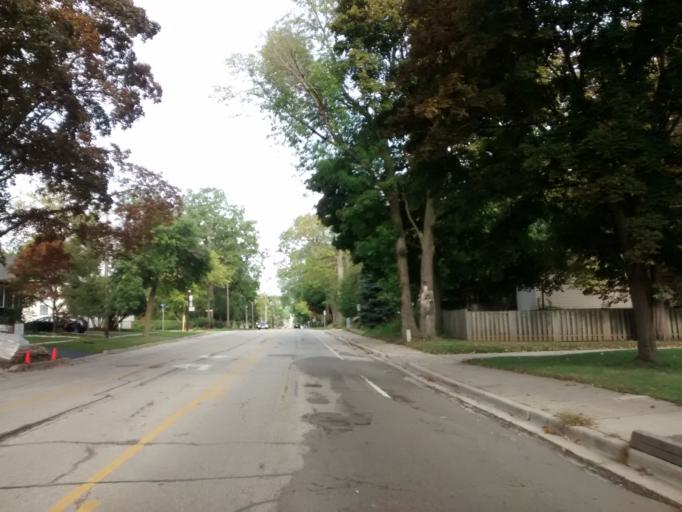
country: CA
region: Ontario
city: Burlington
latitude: 43.3335
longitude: -79.7787
